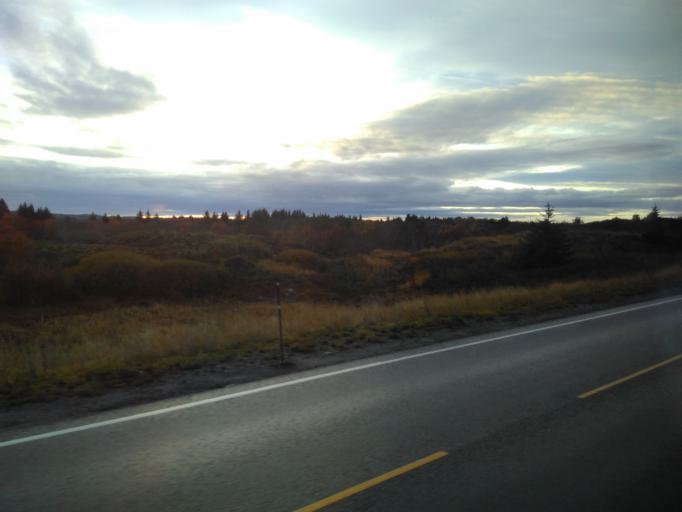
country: NO
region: Sor-Trondelag
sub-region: Froya
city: Sistranda
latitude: 63.6487
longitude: 8.8234
